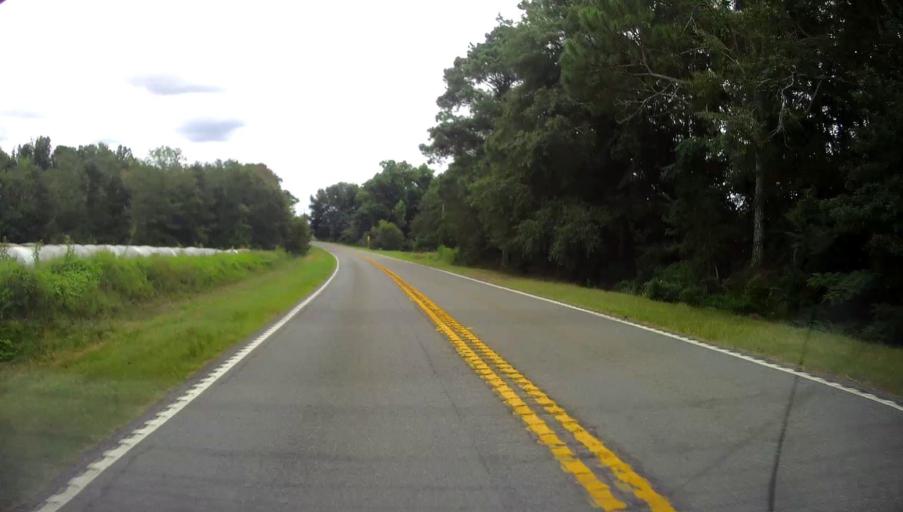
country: US
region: Georgia
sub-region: Dooly County
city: Unadilla
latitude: 32.2596
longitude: -83.8031
